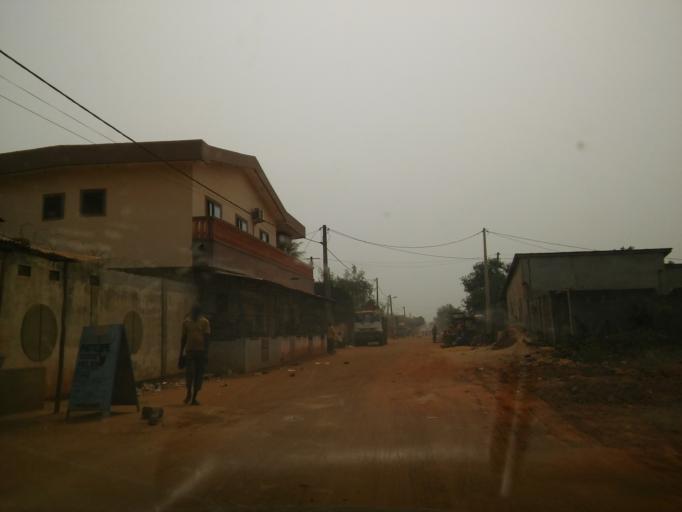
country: BJ
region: Mono
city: Come
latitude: 6.4095
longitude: 1.8776
